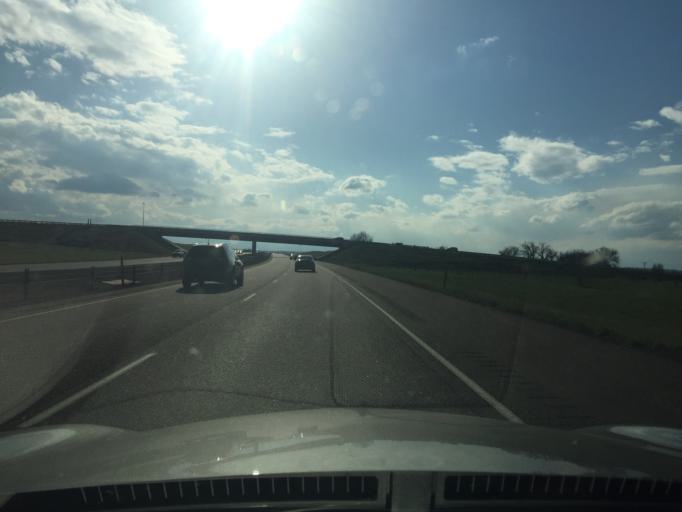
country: US
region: Colorado
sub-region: Adams County
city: Brighton
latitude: 39.9284
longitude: -104.8157
